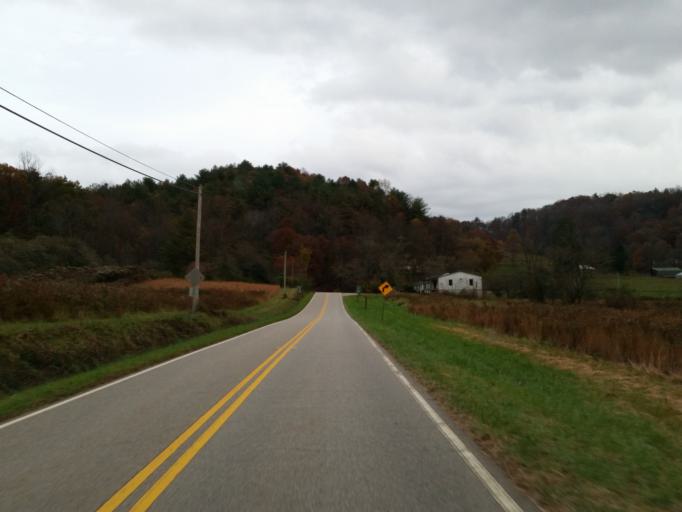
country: US
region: Georgia
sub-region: Union County
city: Blairsville
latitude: 34.7157
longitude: -84.0656
